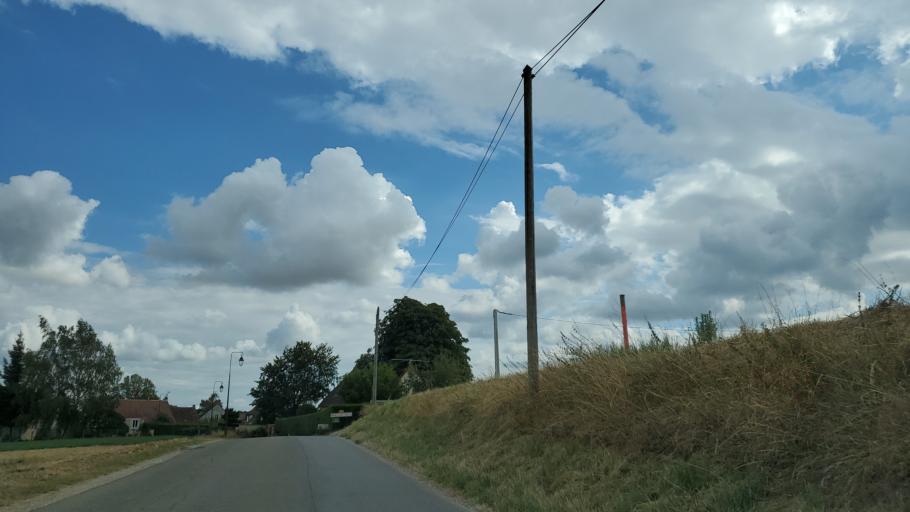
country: FR
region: Ile-de-France
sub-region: Departement de Seine-et-Marne
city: Chailly-en-Brie
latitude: 48.7791
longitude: 3.1630
